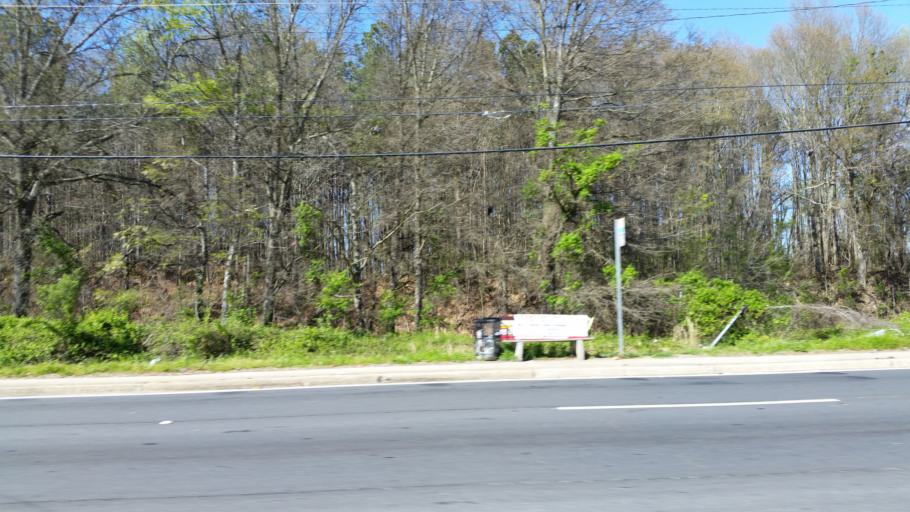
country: US
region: Georgia
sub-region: Fulton County
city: East Point
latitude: 33.7542
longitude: -84.4763
